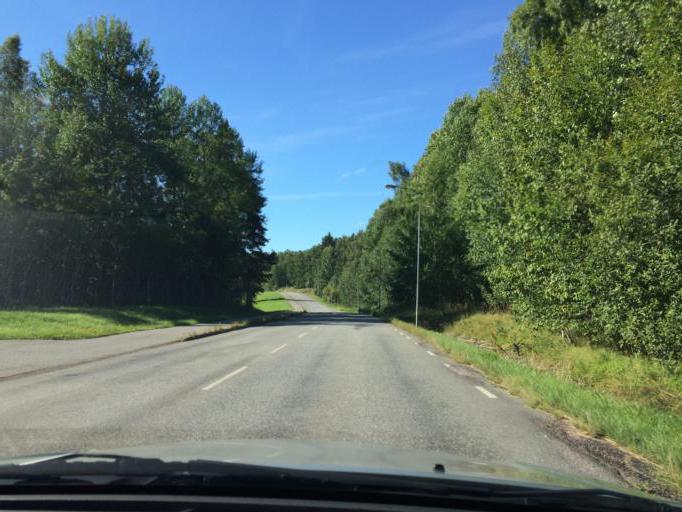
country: SE
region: Vaestmanland
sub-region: Vasteras
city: Vasteras
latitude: 59.5996
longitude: 16.6253
